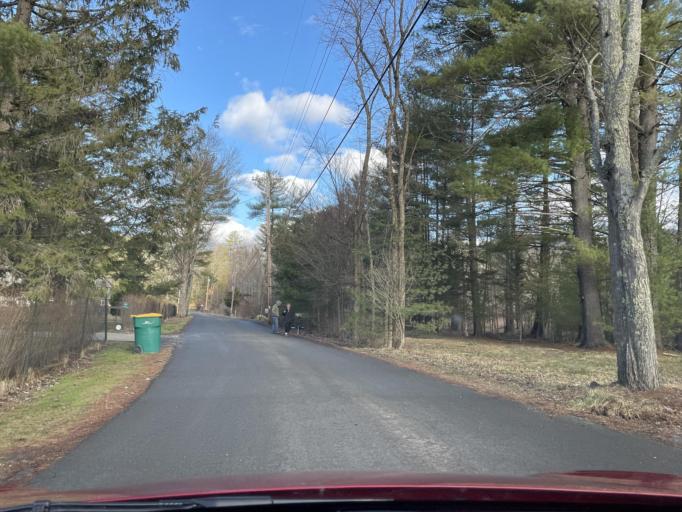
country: US
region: New York
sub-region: Ulster County
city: Woodstock
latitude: 42.0426
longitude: -74.1222
